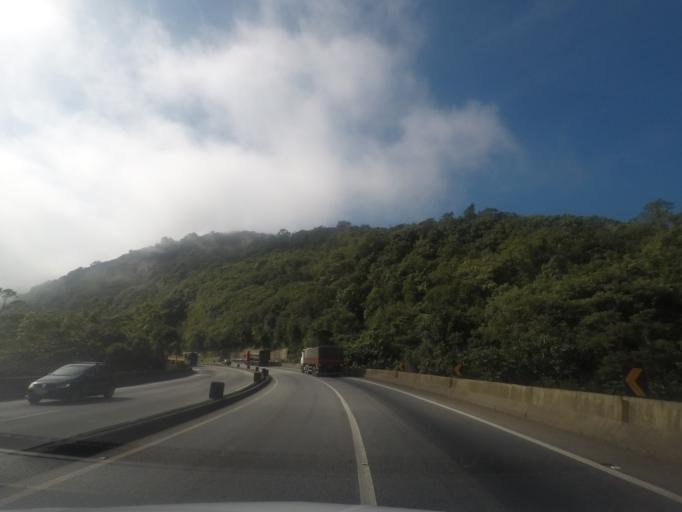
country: BR
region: Parana
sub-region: Piraquara
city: Piraquara
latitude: -25.5936
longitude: -48.8853
